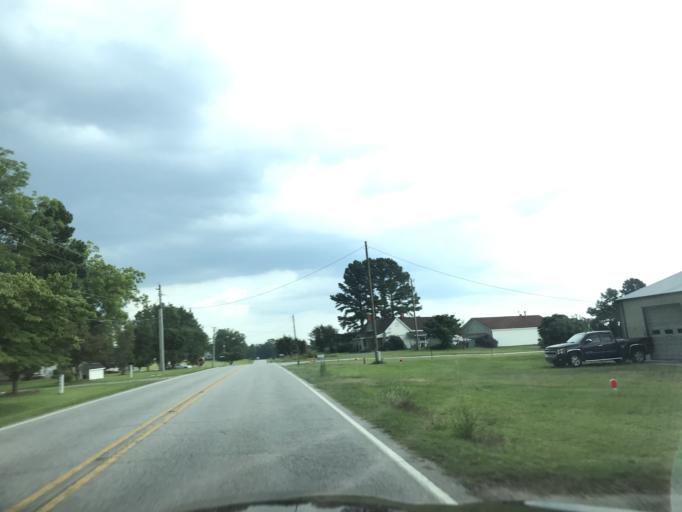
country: US
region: North Carolina
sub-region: Johnston County
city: Four Oaks
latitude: 35.5117
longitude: -78.4801
